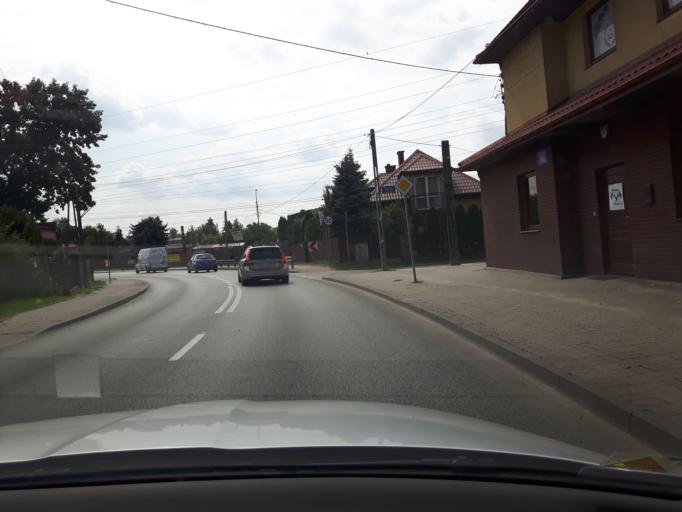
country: PL
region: Masovian Voivodeship
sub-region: Warszawa
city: Rembertow
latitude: 52.2522
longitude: 21.1285
